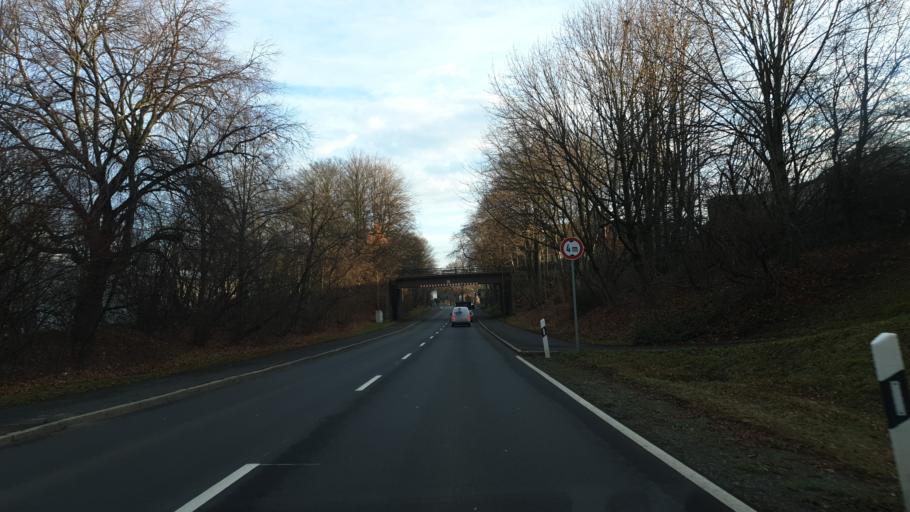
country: DE
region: Saxony
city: Kirchberg
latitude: 50.7930
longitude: 12.7824
